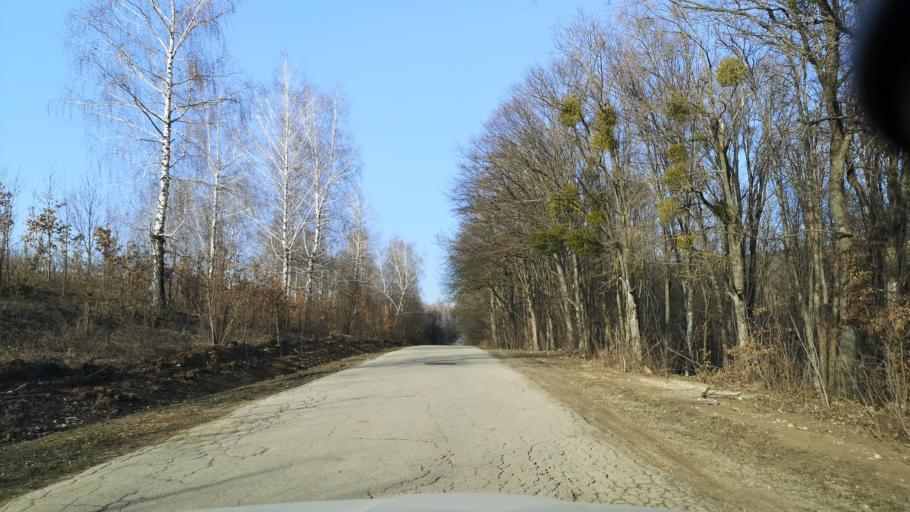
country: MD
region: Nisporeni
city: Nisporeni
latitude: 47.0917
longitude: 28.3159
